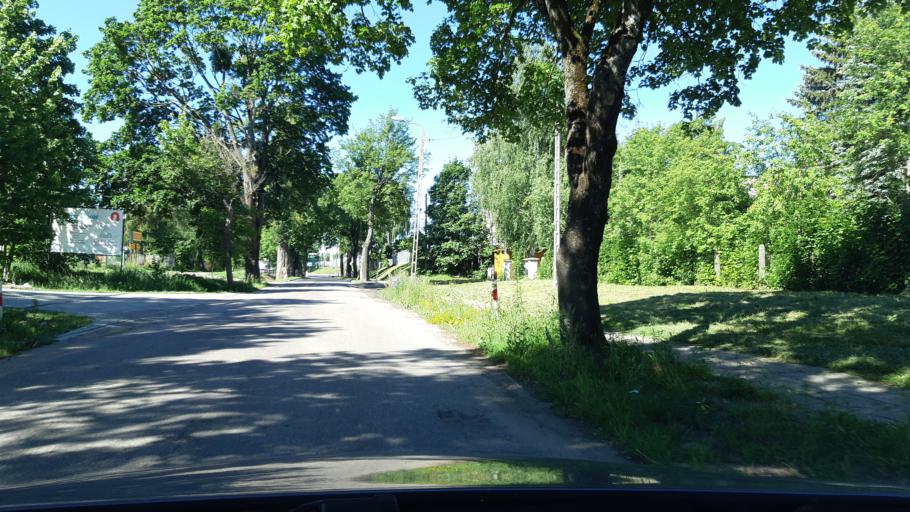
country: PL
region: Warmian-Masurian Voivodeship
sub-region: Powiat mragowski
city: Mragowo
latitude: 53.8545
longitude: 21.2945
